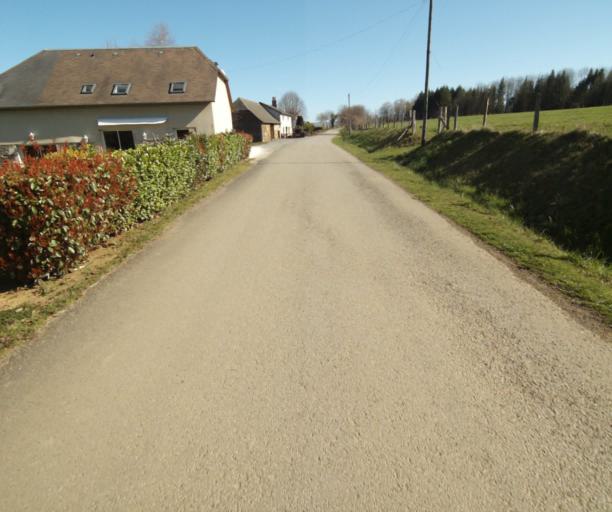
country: FR
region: Limousin
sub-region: Departement de la Correze
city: Seilhac
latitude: 45.3844
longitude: 1.7543
